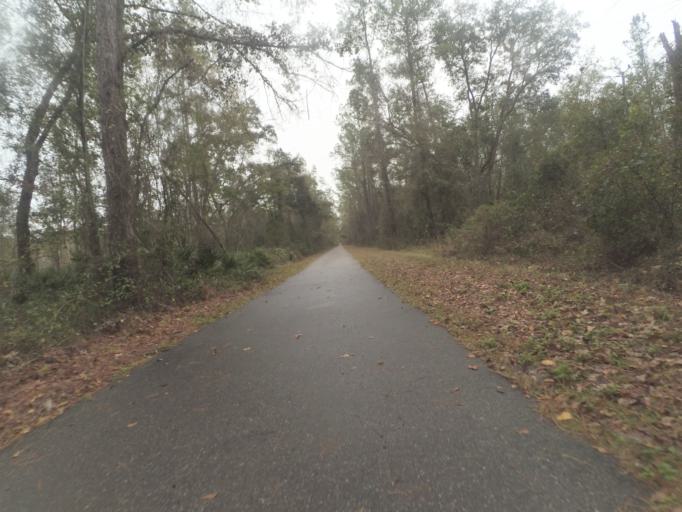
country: US
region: Florida
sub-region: Alachua County
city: Hawthorne
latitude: 29.5980
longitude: -82.1477
